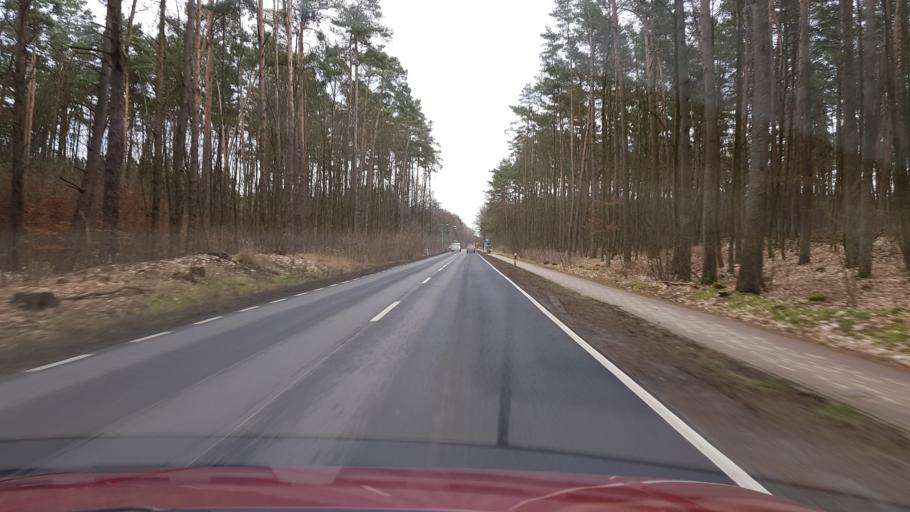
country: PL
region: West Pomeranian Voivodeship
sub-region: Powiat policki
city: Police
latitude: 53.5453
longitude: 14.4997
